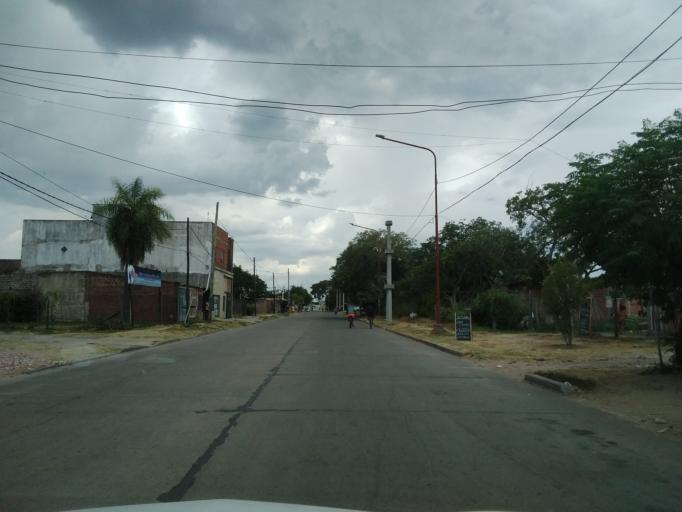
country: AR
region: Corrientes
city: Corrientes
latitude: -27.5248
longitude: -58.7958
